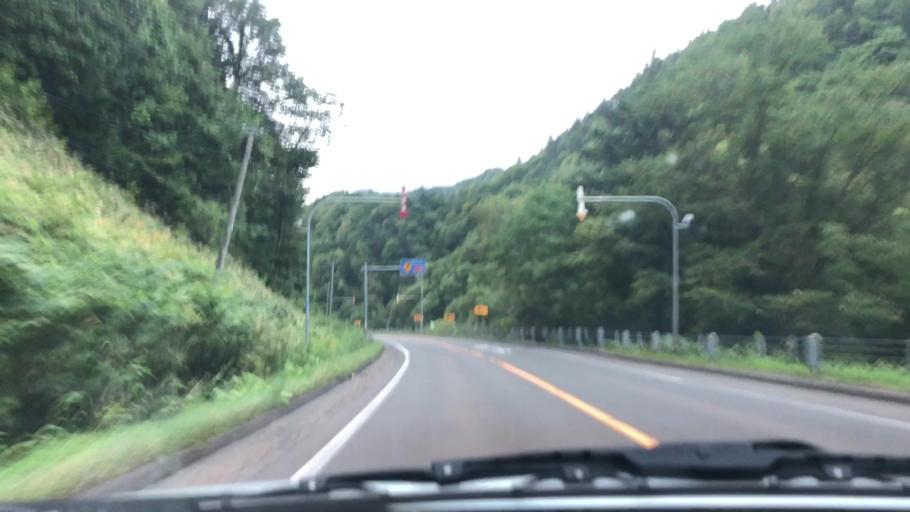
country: JP
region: Hokkaido
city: Iwamizawa
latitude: 42.9266
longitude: 142.1157
